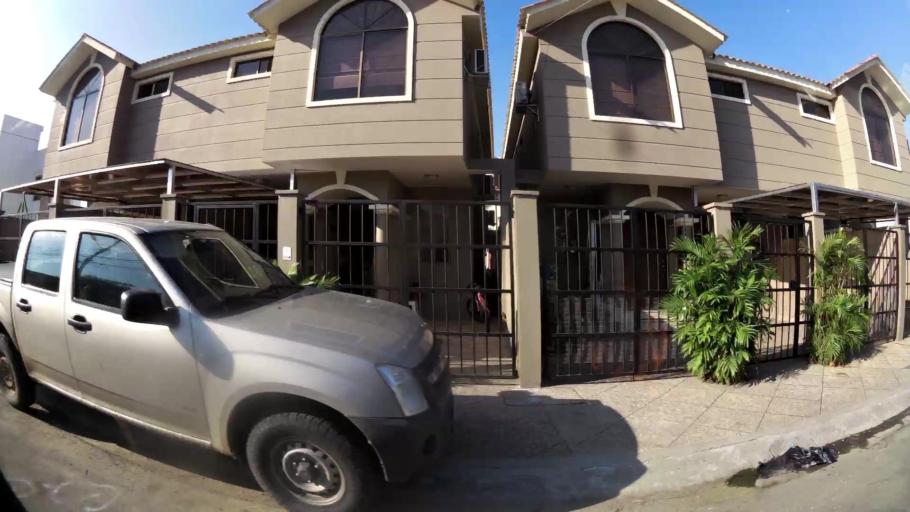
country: EC
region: Guayas
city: Santa Lucia
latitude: -2.1920
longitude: -79.9663
